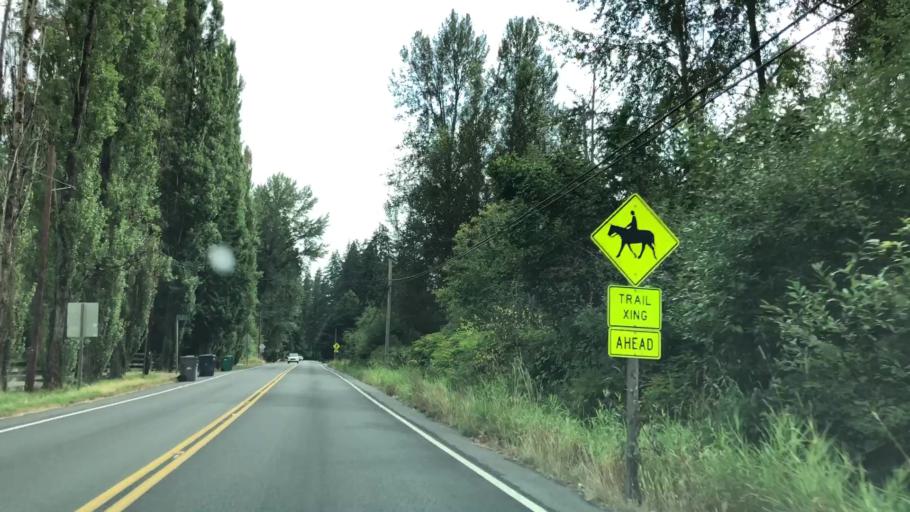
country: US
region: Washington
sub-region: King County
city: Cottage Lake
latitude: 47.7378
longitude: -122.0745
